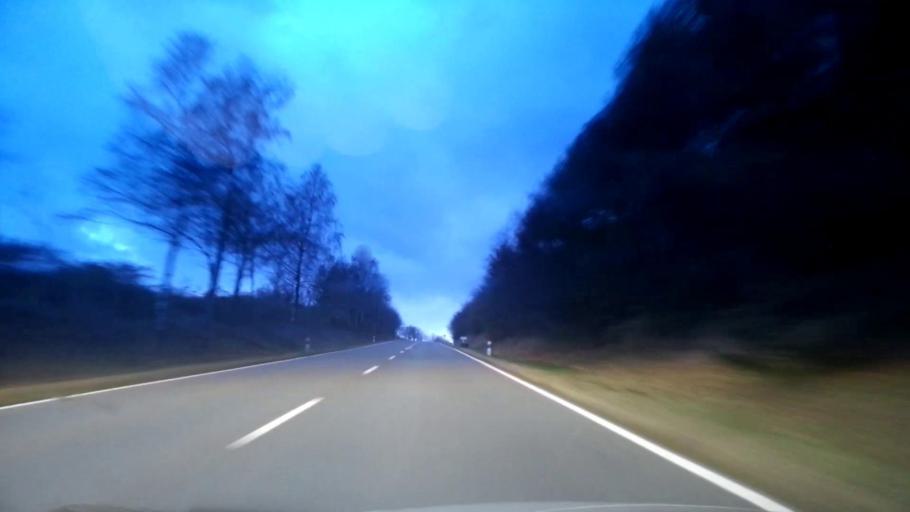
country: DE
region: Bavaria
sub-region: Upper Palatinate
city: Fuchsmuhl
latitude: 49.9389
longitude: 12.1241
